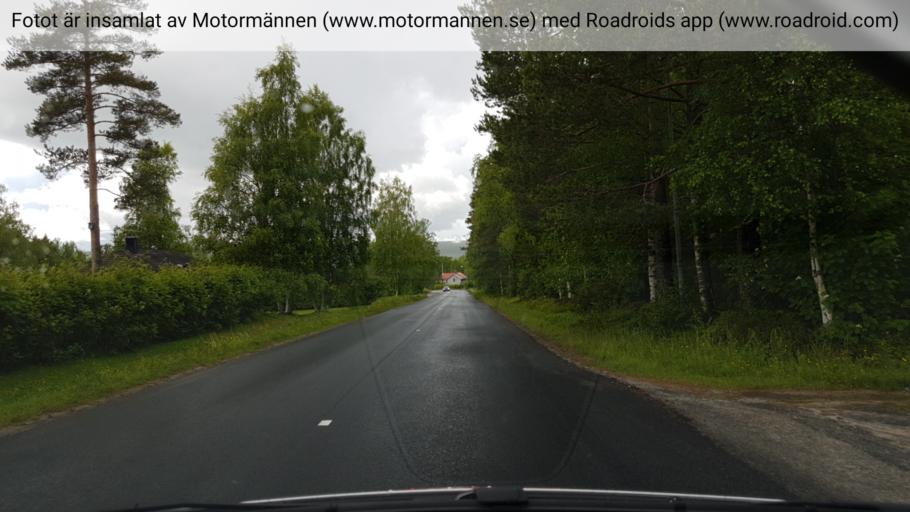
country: SE
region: Vaesterbotten
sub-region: Vannas Kommun
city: Vannasby
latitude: 63.8511
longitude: 19.9340
